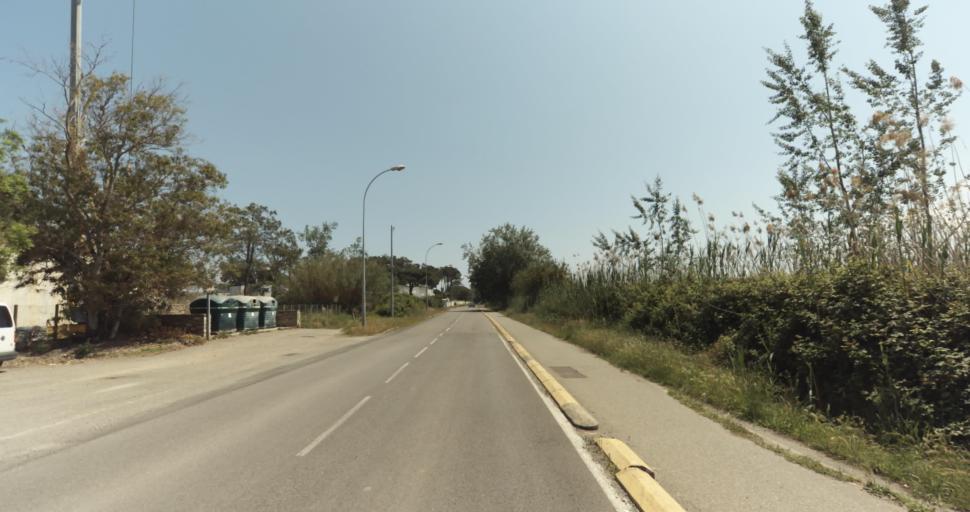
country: FR
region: Corsica
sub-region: Departement de la Haute-Corse
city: Biguglia
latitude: 42.6103
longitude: 9.4831
